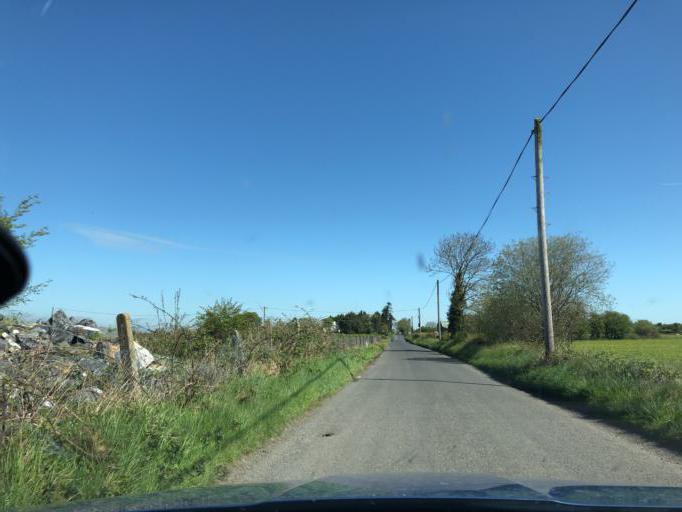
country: IE
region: Connaught
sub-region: County Galway
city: Portumna
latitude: 53.1572
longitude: -8.2959
